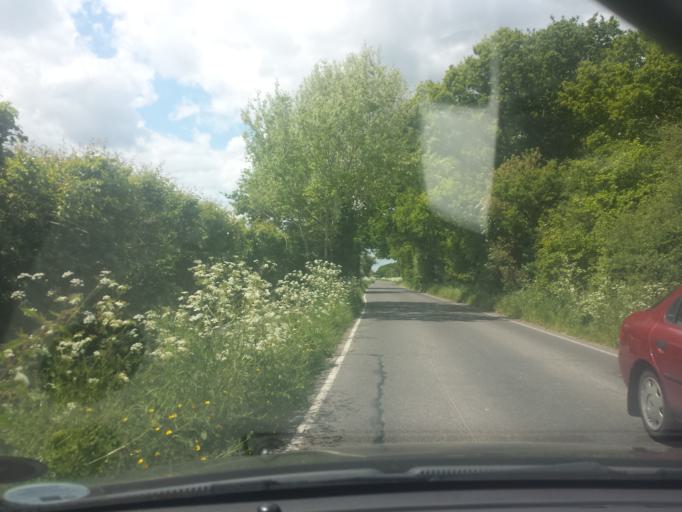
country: GB
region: England
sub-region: Essex
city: Little Clacton
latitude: 51.8873
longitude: 1.1591
